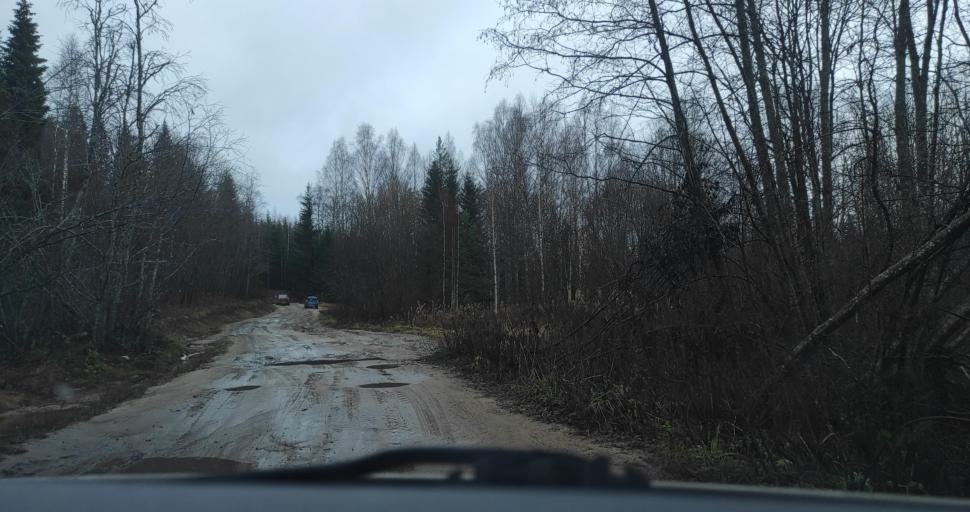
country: RU
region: Republic of Karelia
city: Pitkyaranta
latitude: 61.7472
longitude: 31.3964
